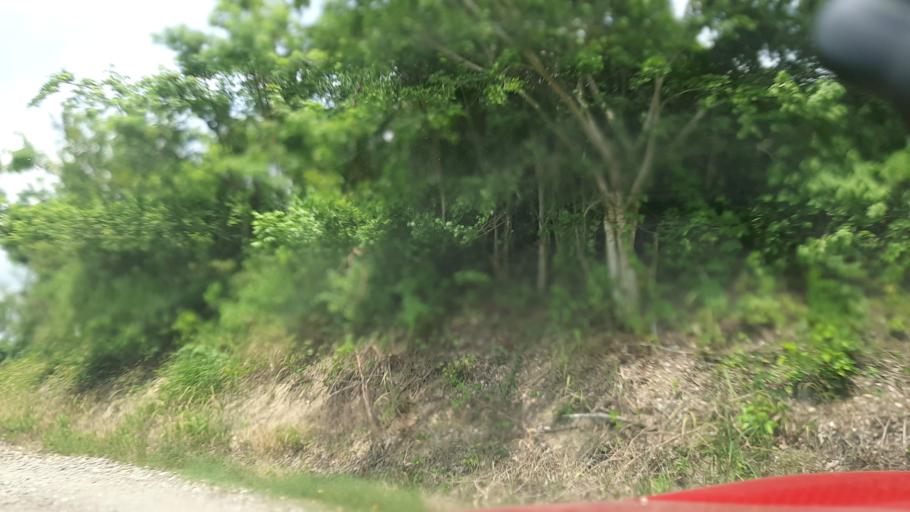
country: MX
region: Veracruz
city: Gutierrez Zamora
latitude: 20.4482
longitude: -97.1760
